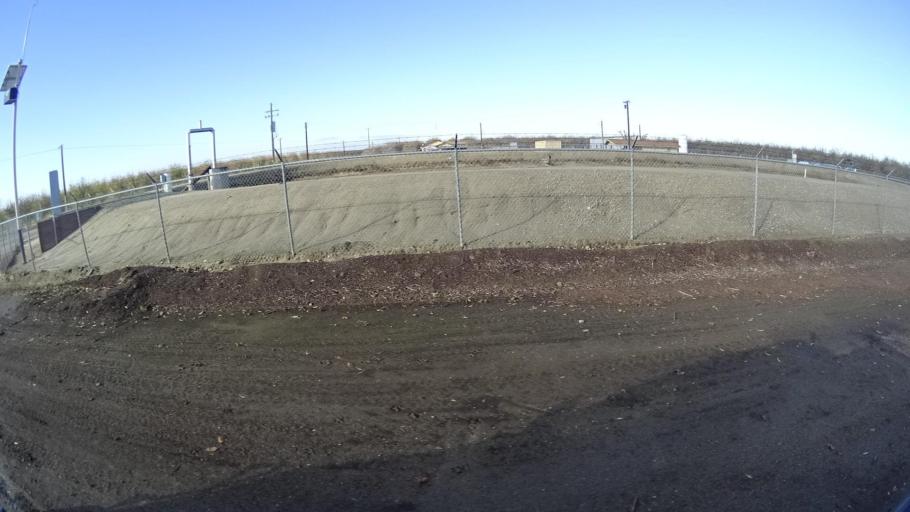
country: US
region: California
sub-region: Kern County
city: McFarland
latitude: 35.7035
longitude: -119.3209
